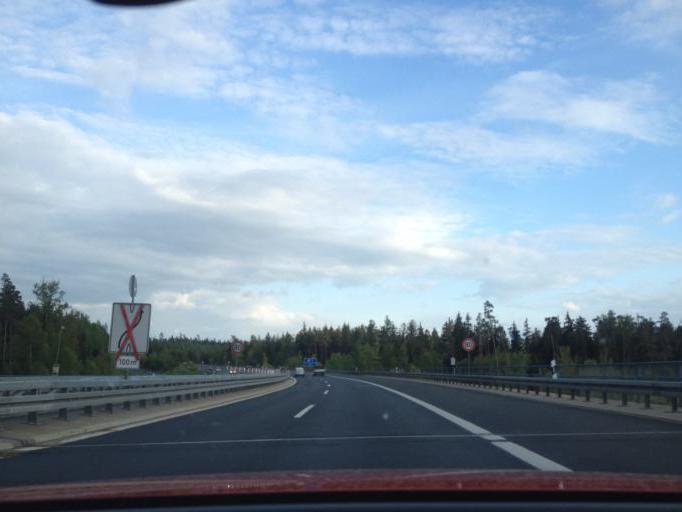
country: DE
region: Bavaria
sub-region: Upper Palatinate
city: Pechbrunn
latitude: 49.9569
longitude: 12.1926
